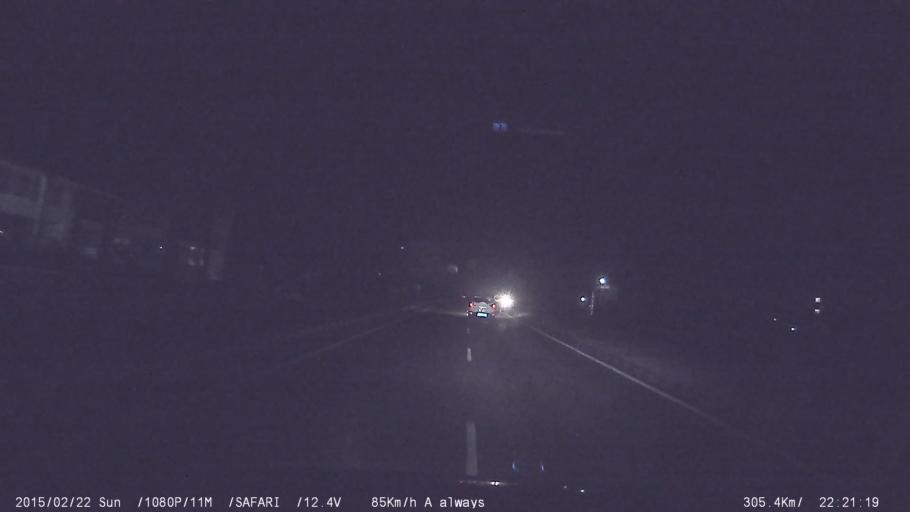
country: IN
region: Tamil Nadu
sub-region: Karur
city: Karur
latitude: 11.0009
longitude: 78.0674
